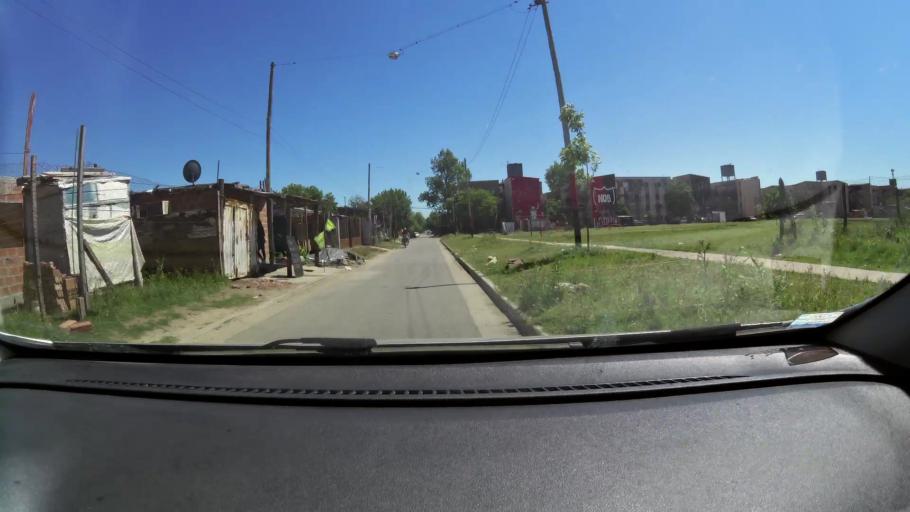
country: AR
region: Santa Fe
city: Perez
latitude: -32.9586
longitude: -60.7199
